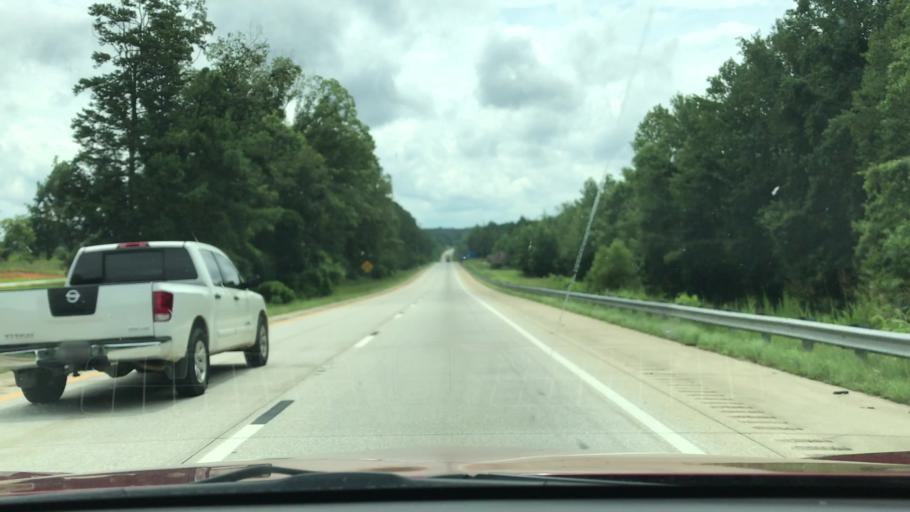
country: US
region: South Carolina
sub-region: Laurens County
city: Clinton
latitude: 34.5159
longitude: -81.8824
